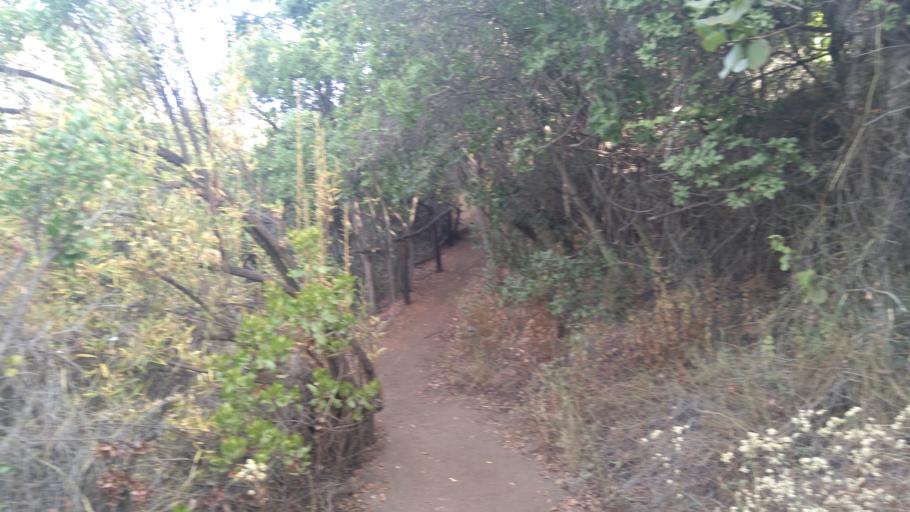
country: CL
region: Santiago Metropolitan
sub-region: Provincia de Cordillera
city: Puente Alto
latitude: -33.7224
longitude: -70.4808
